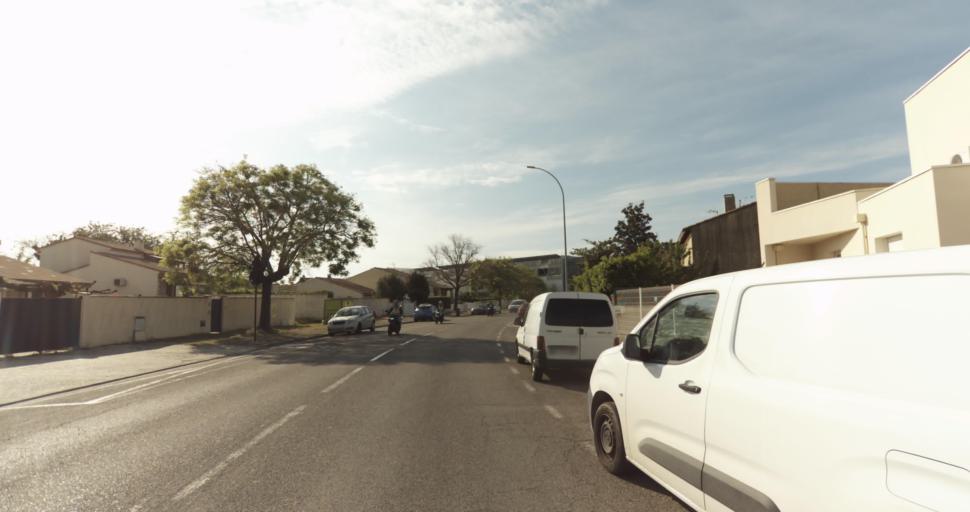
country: FR
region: Languedoc-Roussillon
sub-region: Departement du Gard
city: Rodilhan
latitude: 43.8384
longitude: 4.3912
